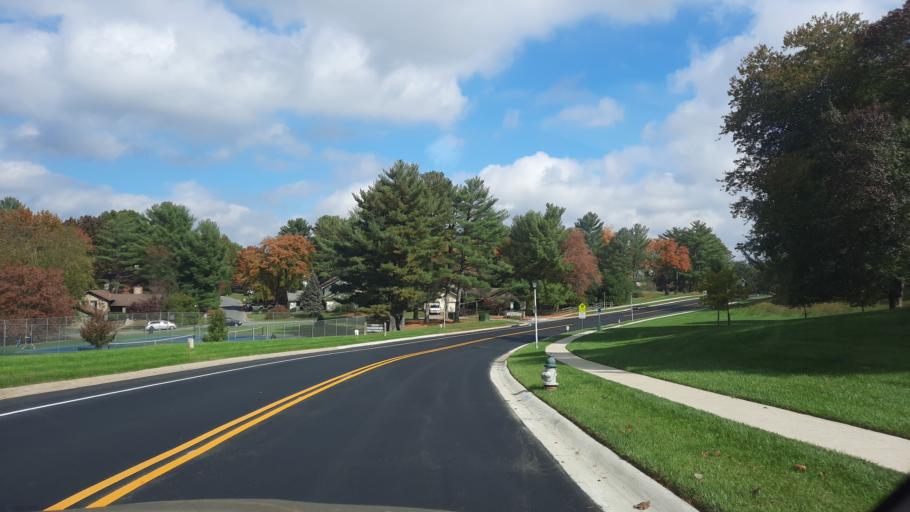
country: US
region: Maryland
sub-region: Montgomery County
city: Montgomery Village
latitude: 39.1739
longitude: -77.2161
